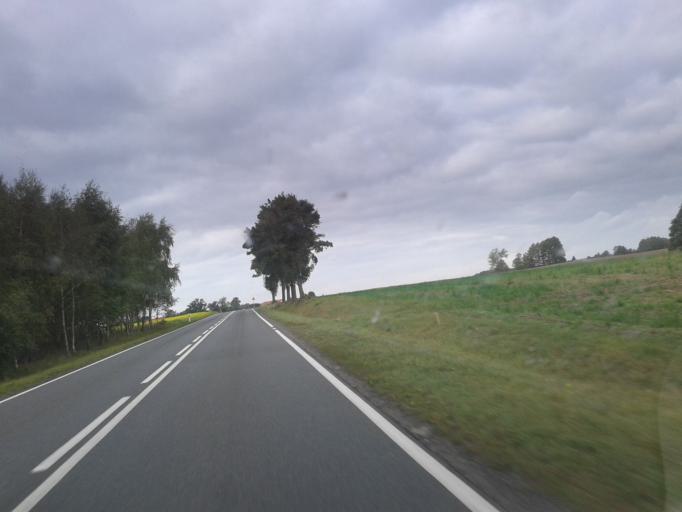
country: PL
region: Kujawsko-Pomorskie
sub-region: Powiat sepolenski
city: Sepolno Krajenskie
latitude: 53.4814
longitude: 17.5209
